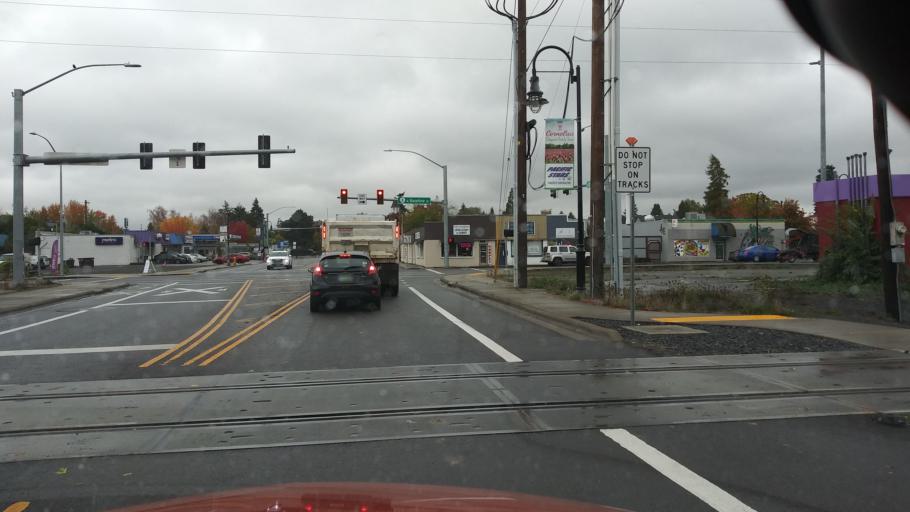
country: US
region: Oregon
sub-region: Washington County
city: Cornelius
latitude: 45.5196
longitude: -123.0595
